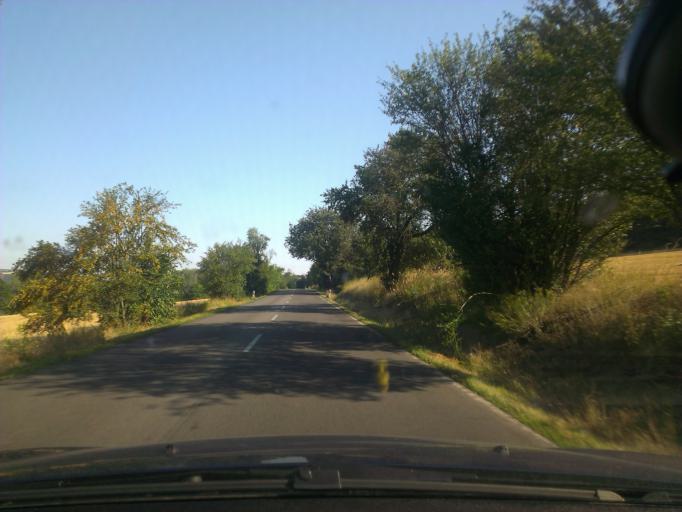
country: SK
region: Trnavsky
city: Vrbove
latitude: 48.6655
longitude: 17.6935
